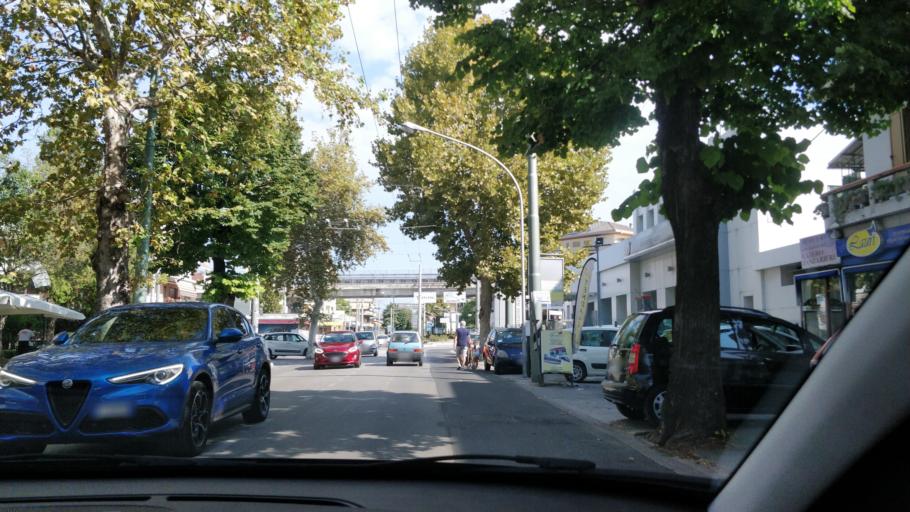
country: IT
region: Abruzzo
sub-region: Provincia di Chieti
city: Chieti
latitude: 42.3716
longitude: 14.1434
